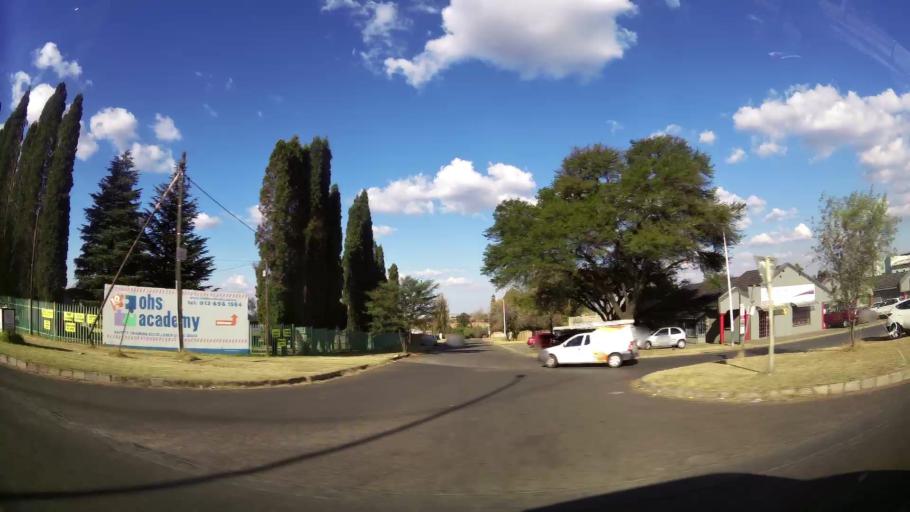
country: ZA
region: Mpumalanga
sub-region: Nkangala District Municipality
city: Witbank
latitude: -25.8788
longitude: 29.2365
